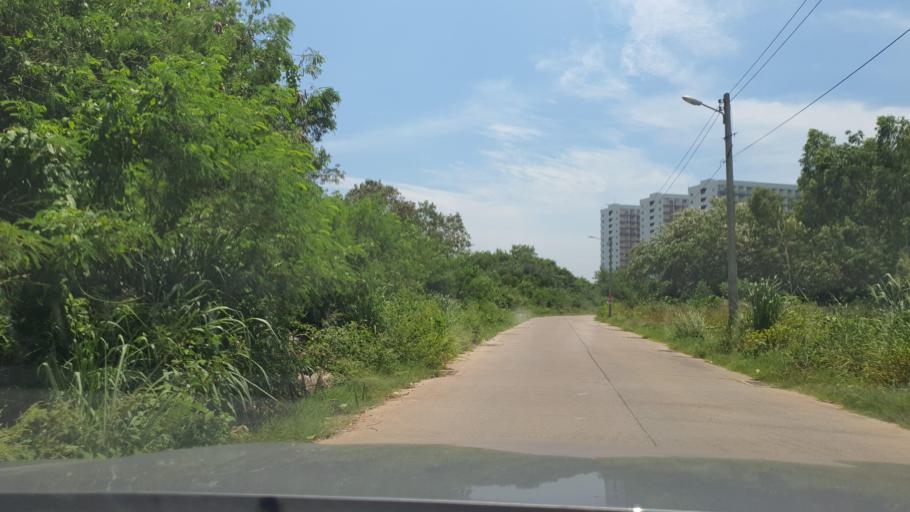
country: TH
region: Chon Buri
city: Phatthaya
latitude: 12.8936
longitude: 100.8814
